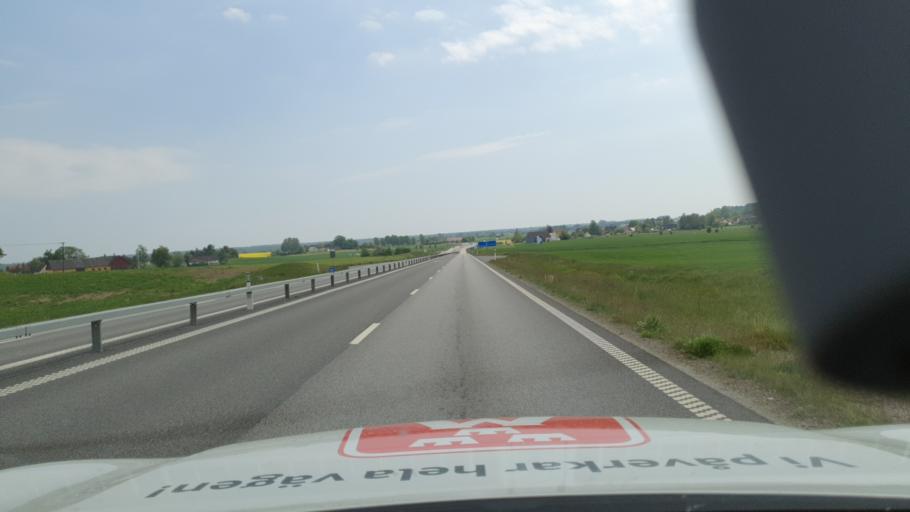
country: SE
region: Skane
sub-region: Ystads Kommun
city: Kopingebro
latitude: 55.4821
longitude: 13.8841
